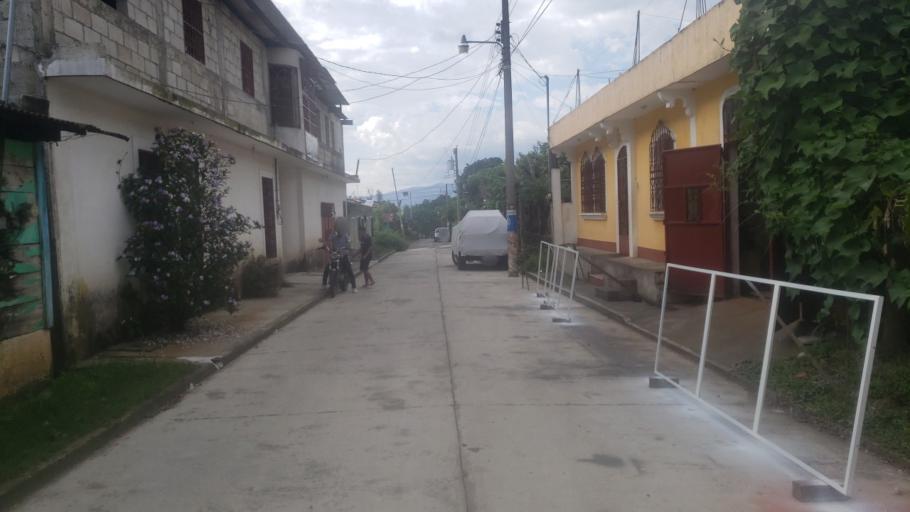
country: GT
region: Suchitepeque
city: Pueblo Nuevo
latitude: 14.6485
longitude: -91.5555
